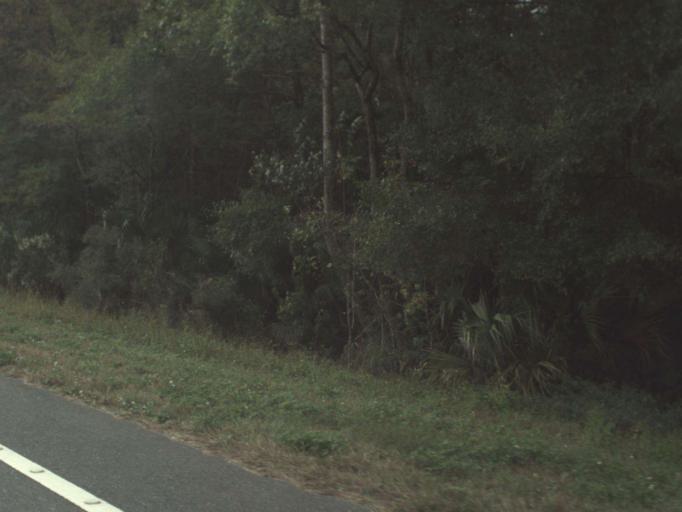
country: US
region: Florida
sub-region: Wakulla County
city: Crawfordville
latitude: 30.1797
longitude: -84.2430
